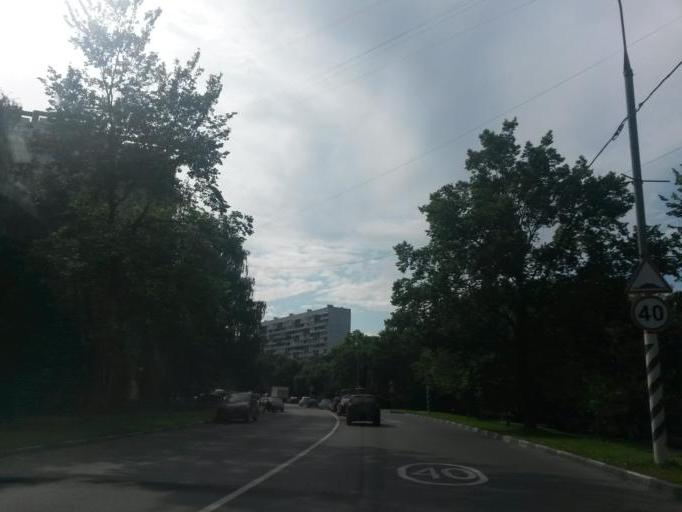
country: RU
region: Moscow
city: Orekhovo-Borisovo
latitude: 55.6261
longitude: 37.7255
